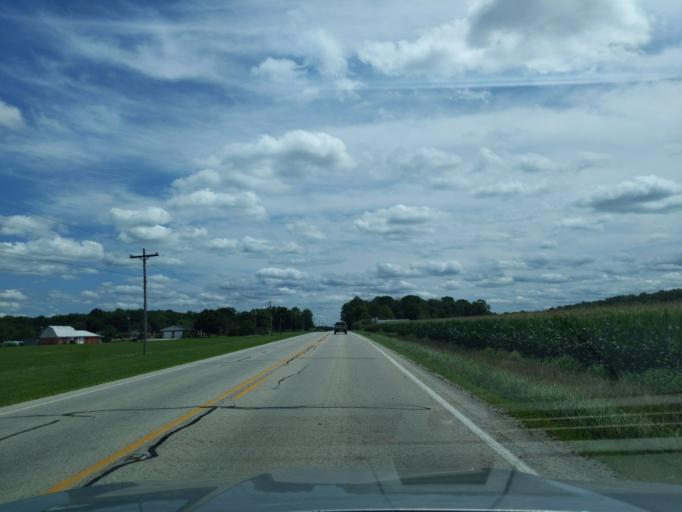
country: US
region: Indiana
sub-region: Ripley County
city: Batesville
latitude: 39.3085
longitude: -85.2918
